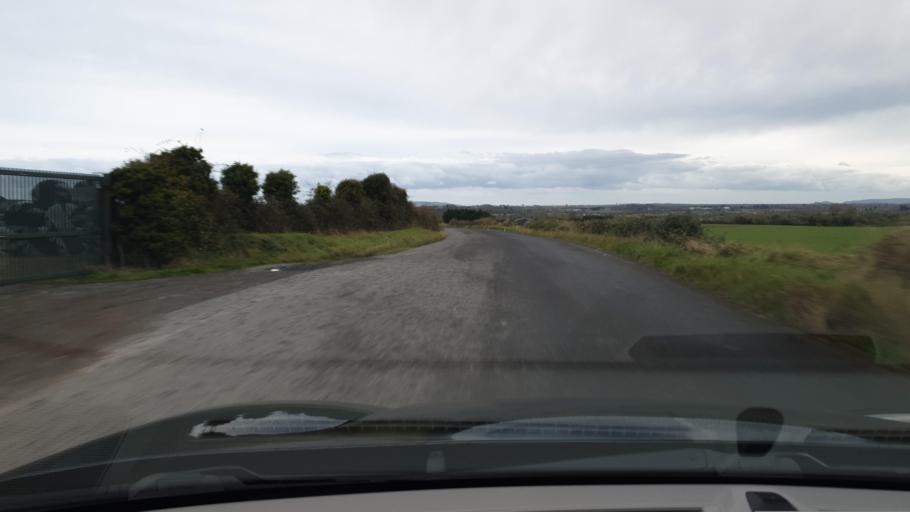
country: IE
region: Leinster
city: Balrothery
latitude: 53.5510
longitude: -6.2318
